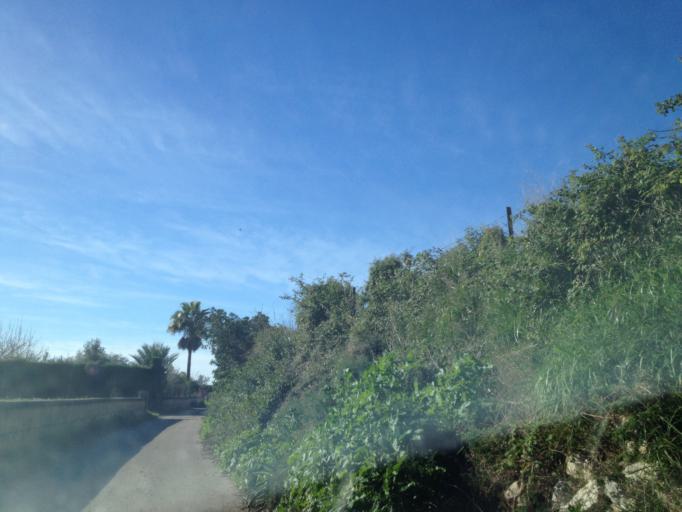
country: ES
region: Balearic Islands
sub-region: Illes Balears
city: Sineu
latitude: 39.6476
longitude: 3.0356
